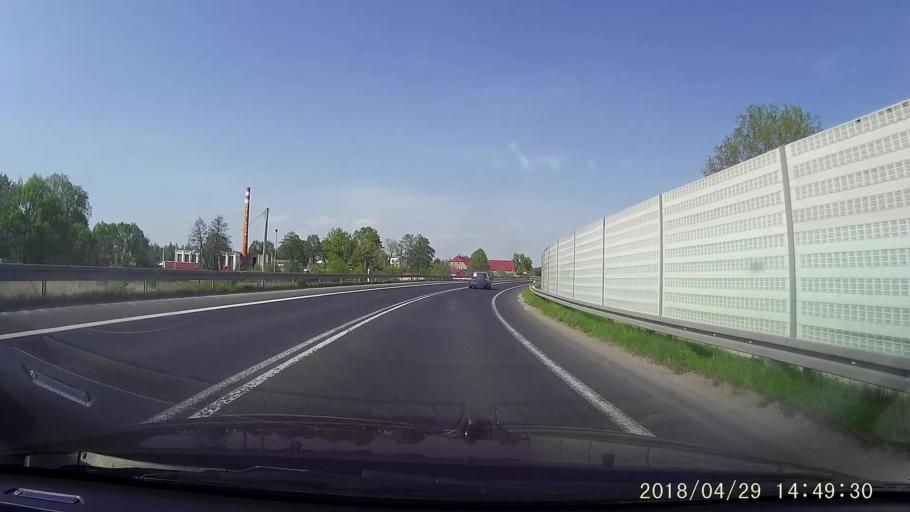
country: PL
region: Lower Silesian Voivodeship
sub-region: Powiat zgorzelecki
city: Zgorzelec
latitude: 51.1304
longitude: 15.0217
